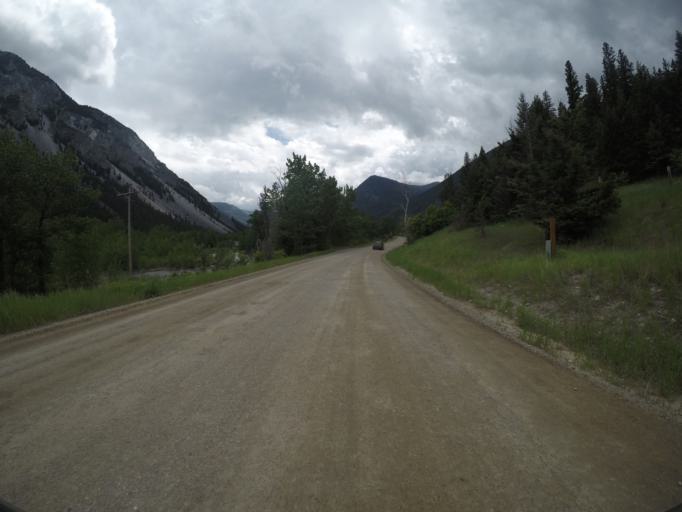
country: US
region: Montana
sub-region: Park County
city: Livingston
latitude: 45.5059
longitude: -110.2264
